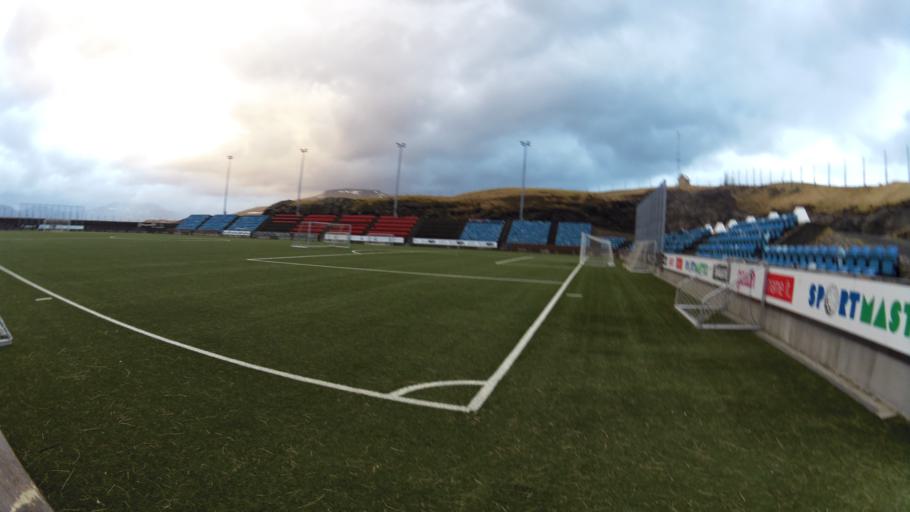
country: FO
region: Streymoy
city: Hoyvik
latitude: 62.1008
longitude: -6.7357
